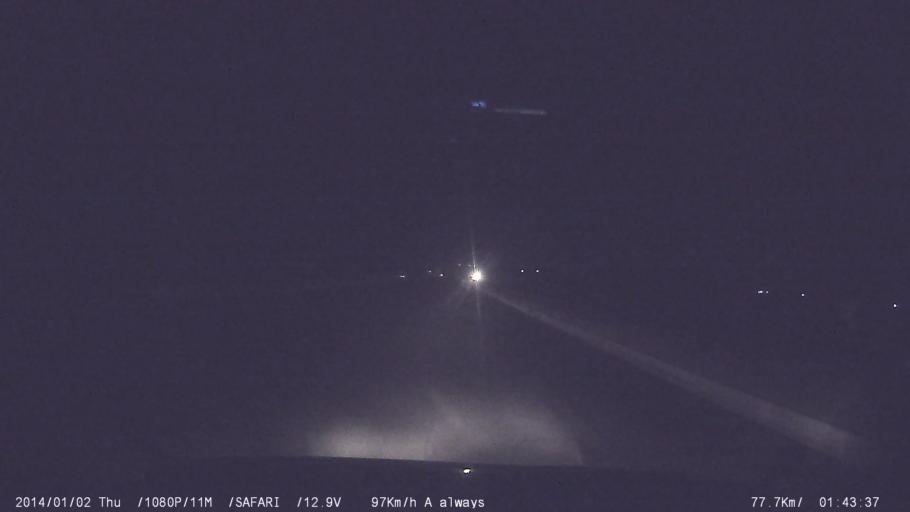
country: IN
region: Tamil Nadu
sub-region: Tiruppur
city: Avinashi
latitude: 11.1766
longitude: 77.2461
